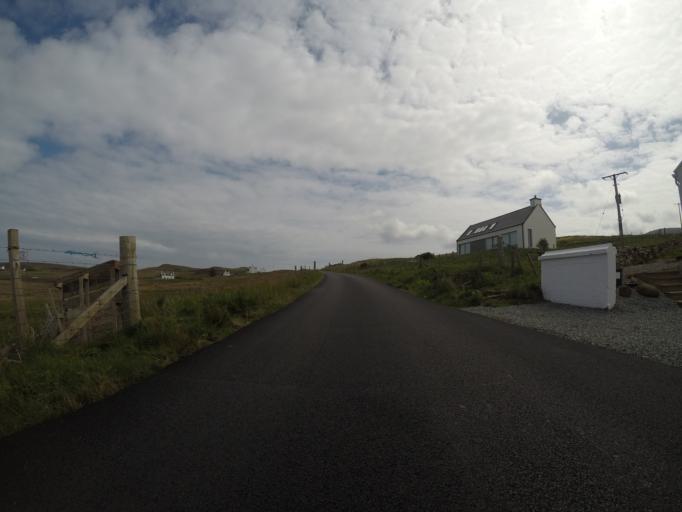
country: GB
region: Scotland
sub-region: Highland
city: Portree
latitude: 57.6827
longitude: -6.2988
